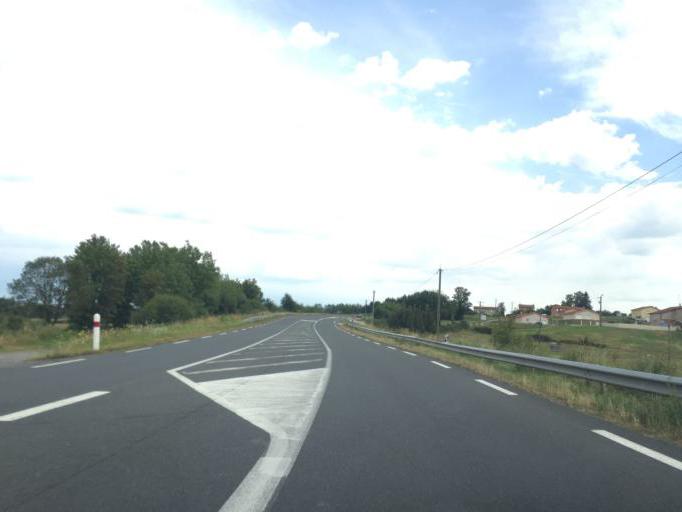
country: FR
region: Rhone-Alpes
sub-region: Departement de la Loire
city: Saint-Symphorien-de-Lay
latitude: 45.9520
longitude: 4.1947
